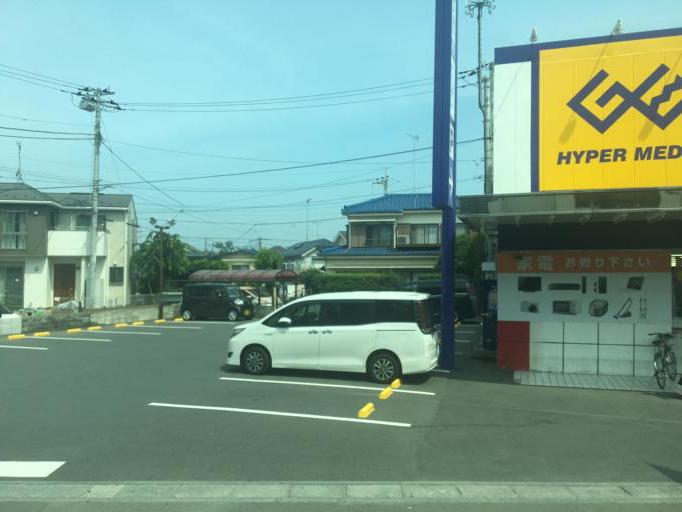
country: JP
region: Tokyo
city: Tanashicho
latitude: 35.7656
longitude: 139.5566
